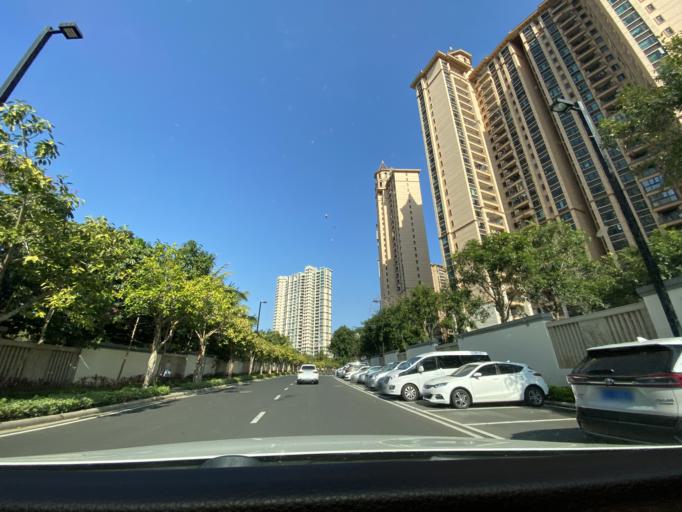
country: CN
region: Hainan
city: Yingzhou
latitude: 18.4127
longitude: 109.8865
